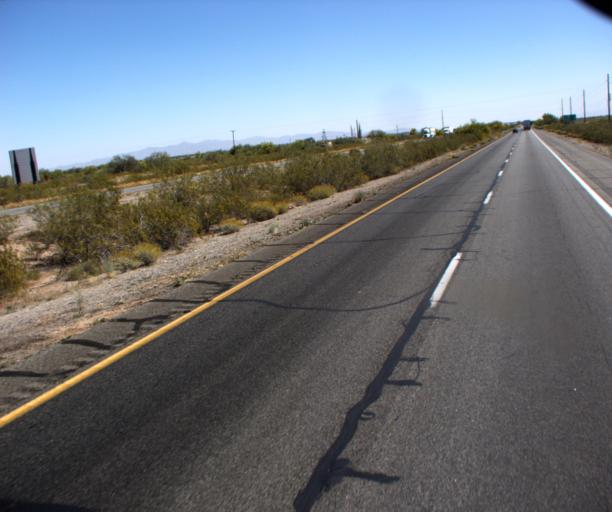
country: US
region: Arizona
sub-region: Maricopa County
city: Buckeye
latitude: 33.4938
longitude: -112.9218
